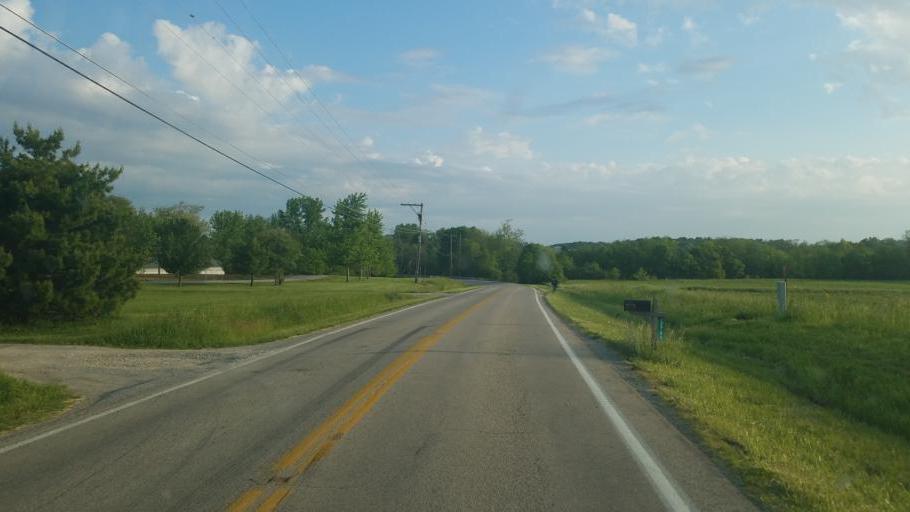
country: US
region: Ohio
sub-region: Highland County
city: Leesburg
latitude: 39.3618
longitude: -83.5898
